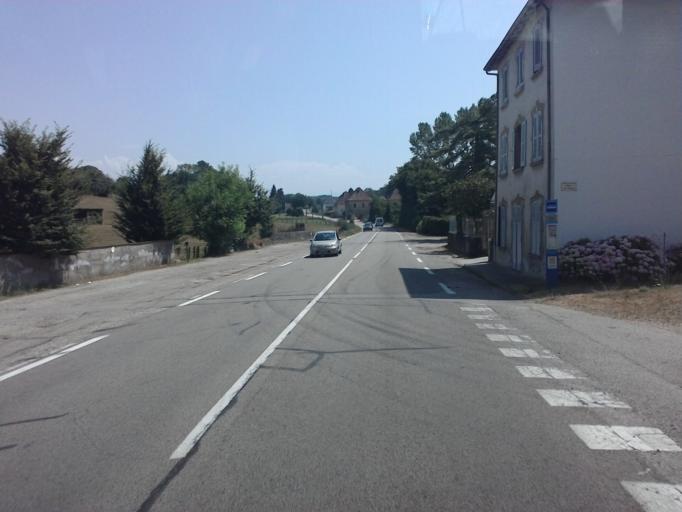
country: FR
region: Rhone-Alpes
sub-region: Departement de l'Isere
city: La Batie-Montgascon
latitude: 45.5881
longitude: 5.5404
